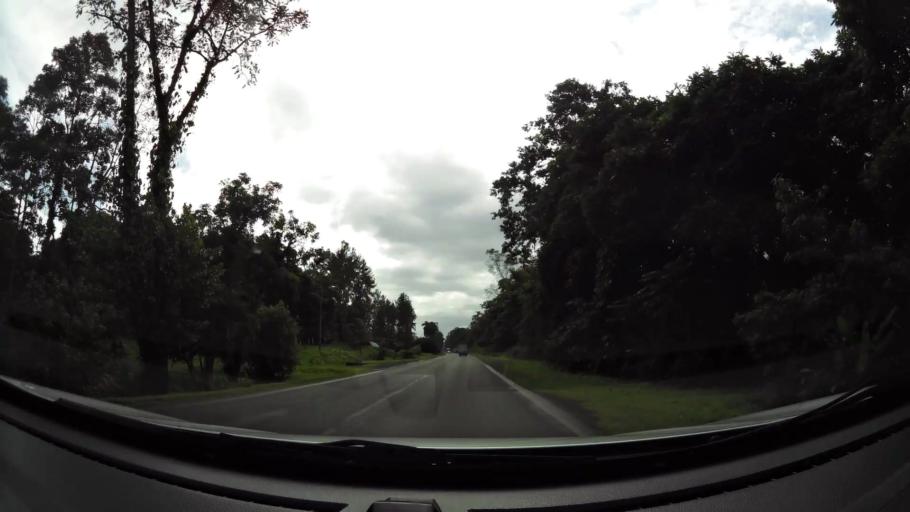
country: CR
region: Limon
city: Pocora
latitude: 10.1836
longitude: -83.6280
